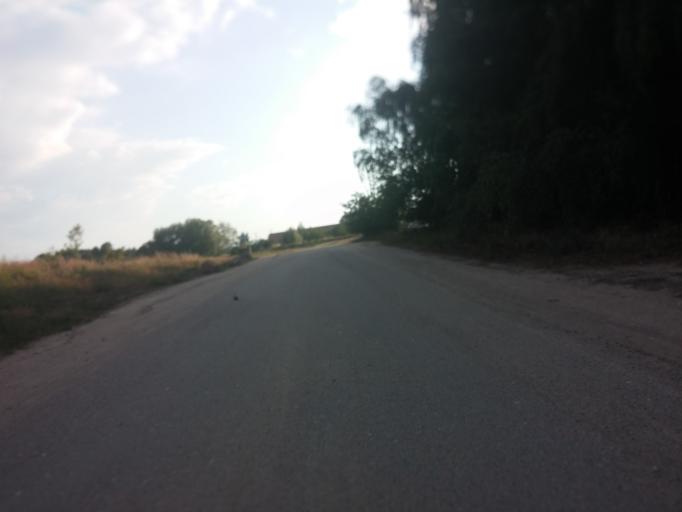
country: CZ
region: Central Bohemia
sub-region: Okres Nymburk
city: Podebrady
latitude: 50.1273
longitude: 15.1211
